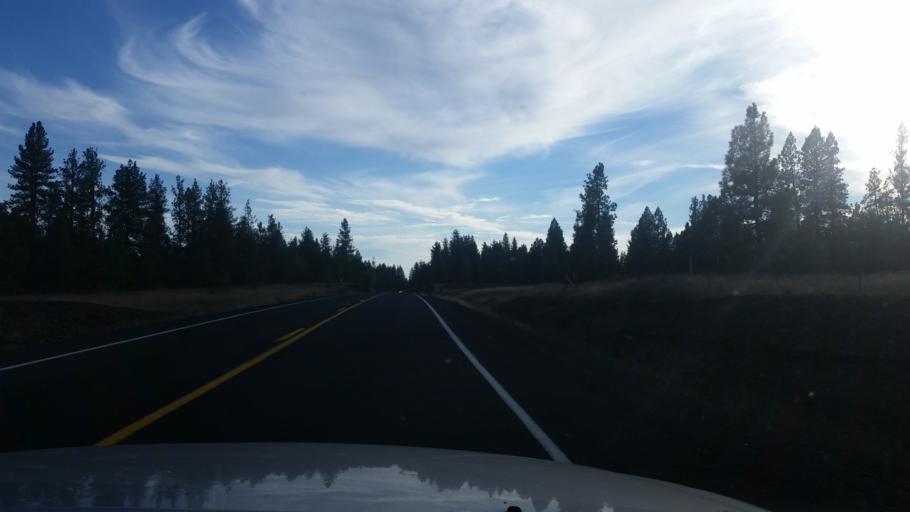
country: US
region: Washington
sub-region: Spokane County
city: Cheney
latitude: 47.4086
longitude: -117.5694
